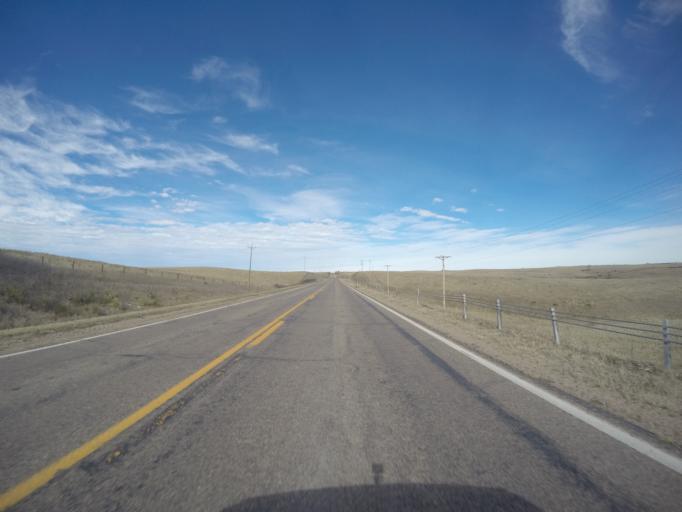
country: US
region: Nebraska
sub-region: Franklin County
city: Franklin
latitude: 40.1442
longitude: -98.9524
